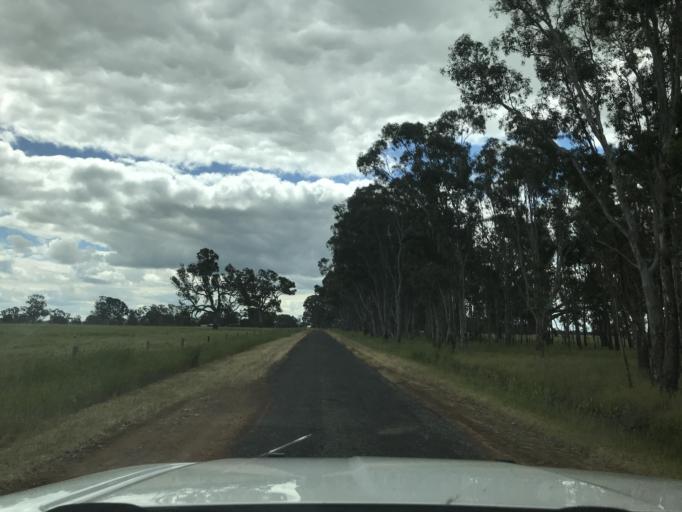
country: AU
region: South Australia
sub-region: Naracoorte and Lucindale
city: Naracoorte
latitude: -37.0736
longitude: 141.1741
